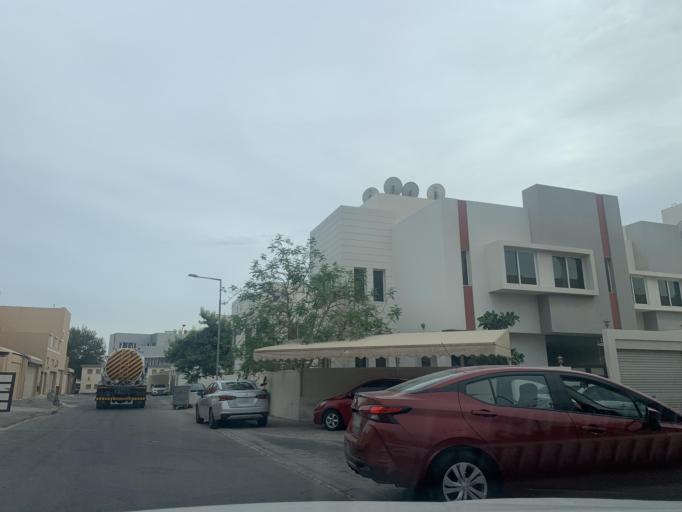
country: BH
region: Muharraq
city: Al Hadd
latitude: 26.2794
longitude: 50.6474
